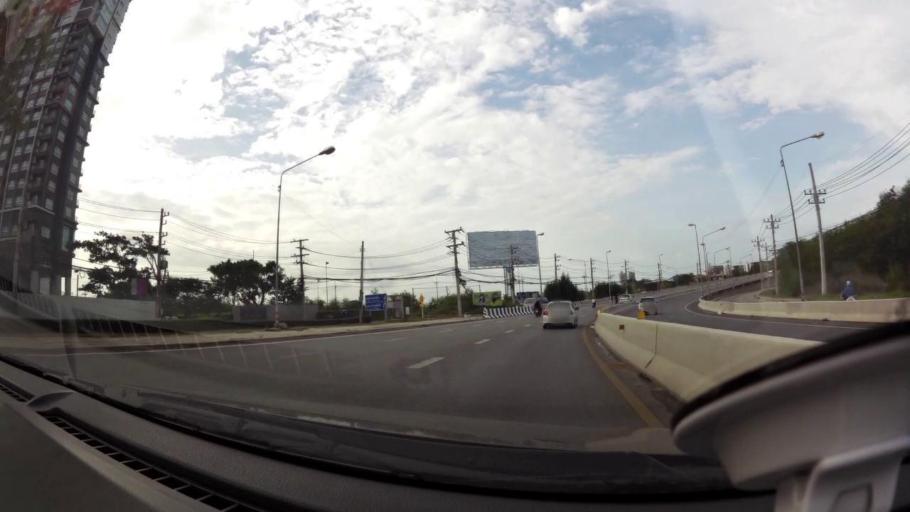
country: TH
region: Prachuap Khiri Khan
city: Hua Hin
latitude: 12.5370
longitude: 99.9595
